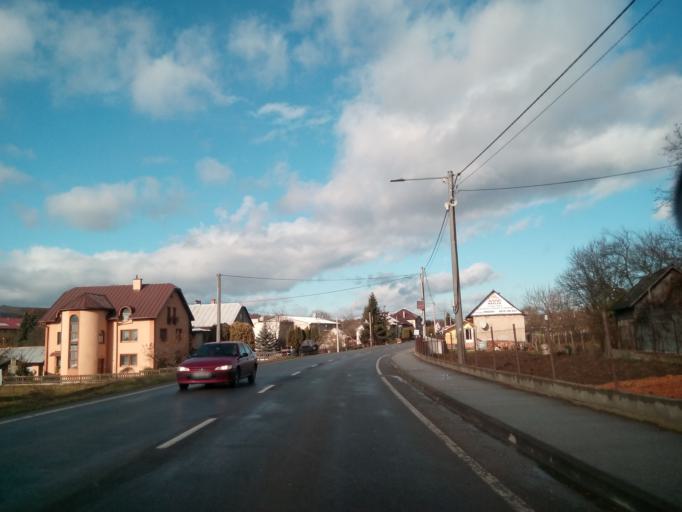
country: SK
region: Presovsky
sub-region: Okres Bardejov
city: Bardejov
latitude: 49.2122
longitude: 21.2983
